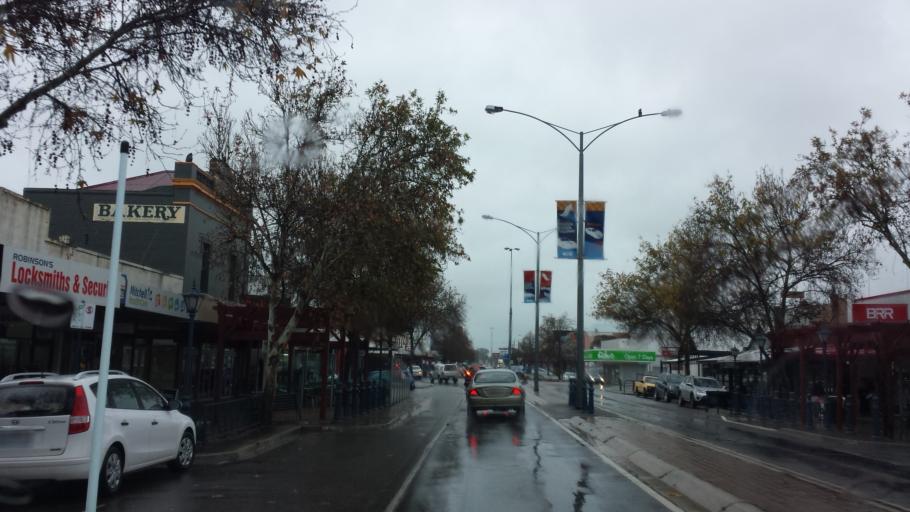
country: AU
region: Victoria
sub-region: Benalla
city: Benalla
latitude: -36.5514
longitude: 145.9845
